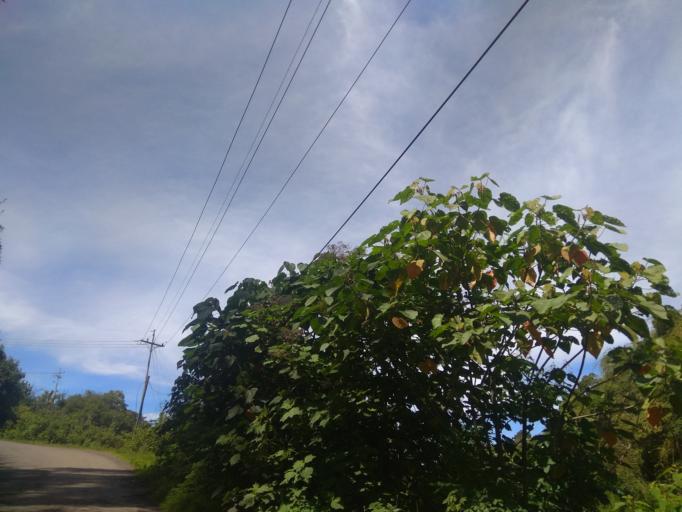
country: CR
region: Cartago
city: Cot
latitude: 9.9227
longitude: -83.9012
